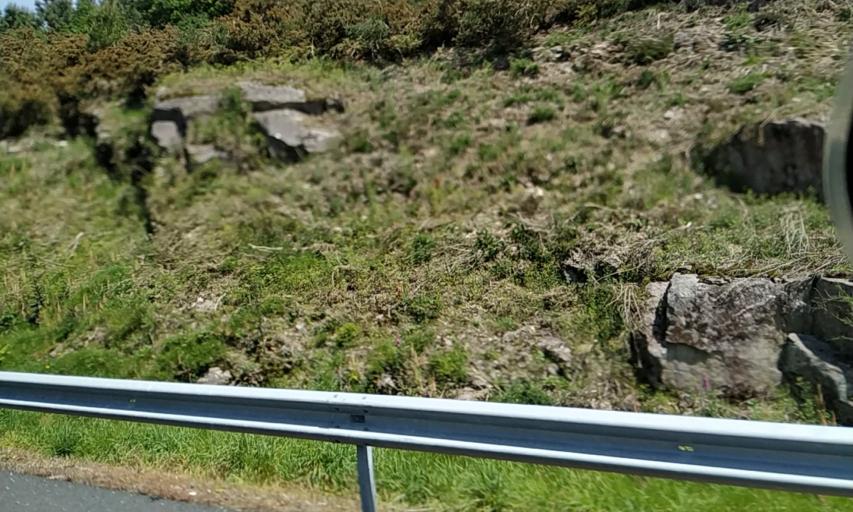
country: ES
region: Galicia
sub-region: Provincia da Coruna
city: Padron
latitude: 42.7528
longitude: -8.6470
